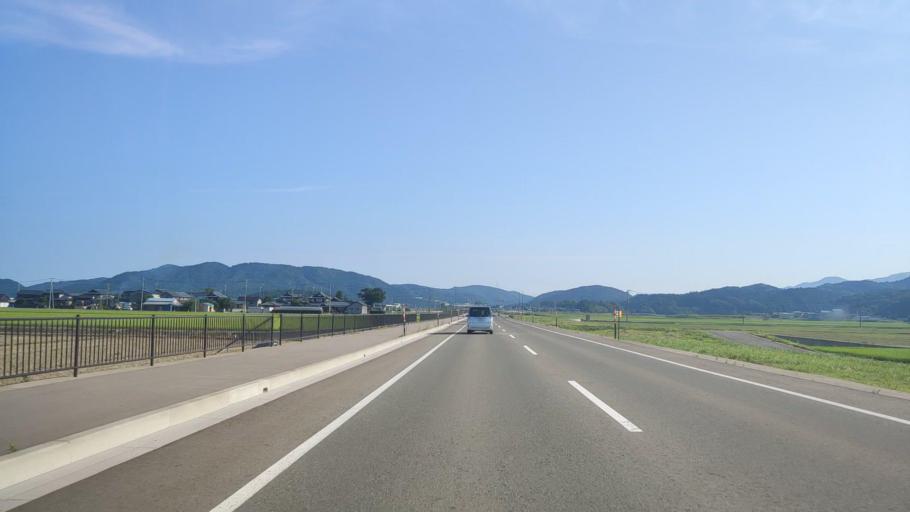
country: JP
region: Fukui
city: Maruoka
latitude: 36.1837
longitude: 136.2680
